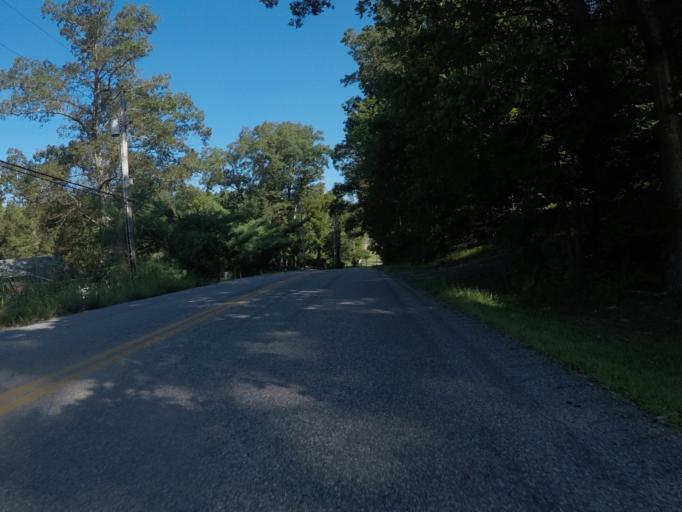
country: US
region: Kentucky
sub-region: Greenup County
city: Russell
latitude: 38.4983
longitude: -82.6964
